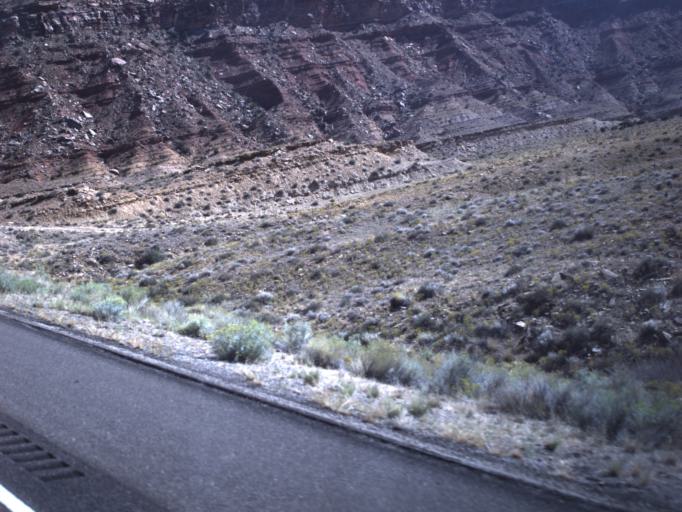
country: US
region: Utah
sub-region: Carbon County
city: East Carbon City
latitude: 38.9269
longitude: -110.4545
